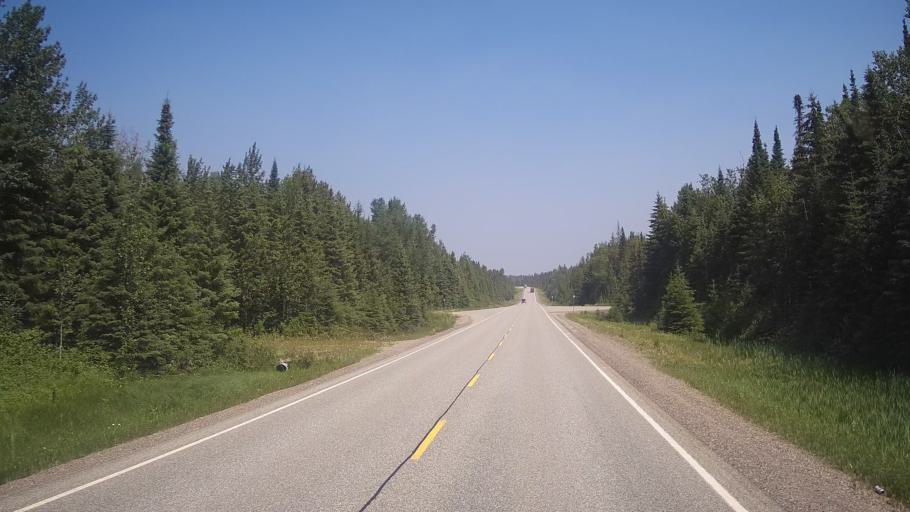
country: CA
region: Ontario
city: Timmins
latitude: 48.0922
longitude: -81.5938
